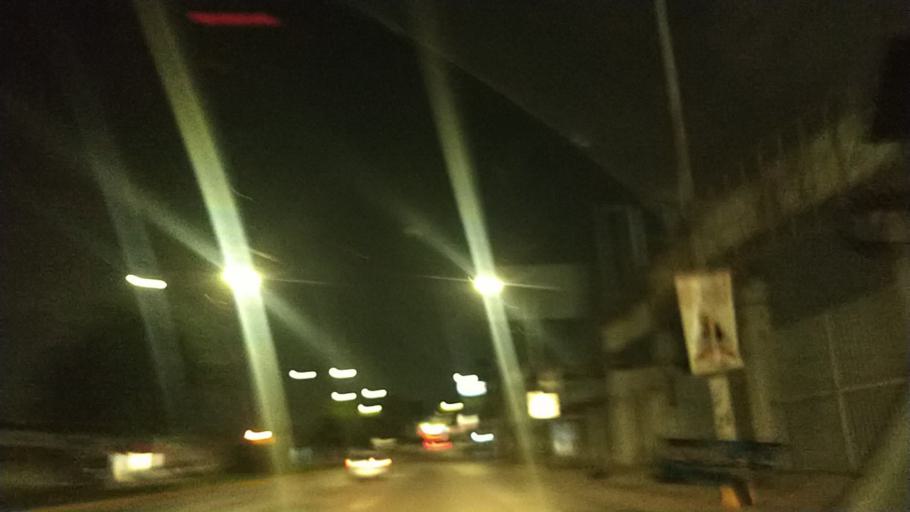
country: MX
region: Mexico
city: Ecatepec
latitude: 19.6213
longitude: -99.0717
